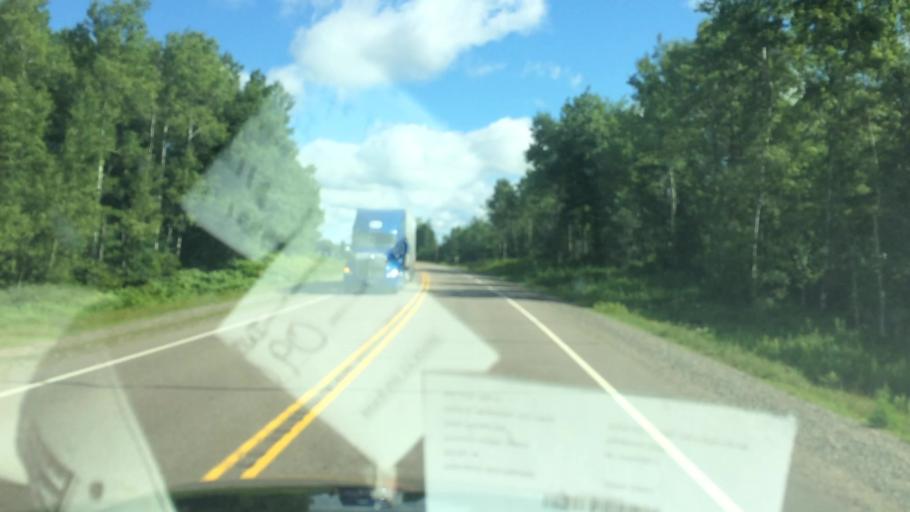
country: US
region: Wisconsin
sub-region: Oneida County
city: Rhinelander
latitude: 45.5742
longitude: -89.5707
